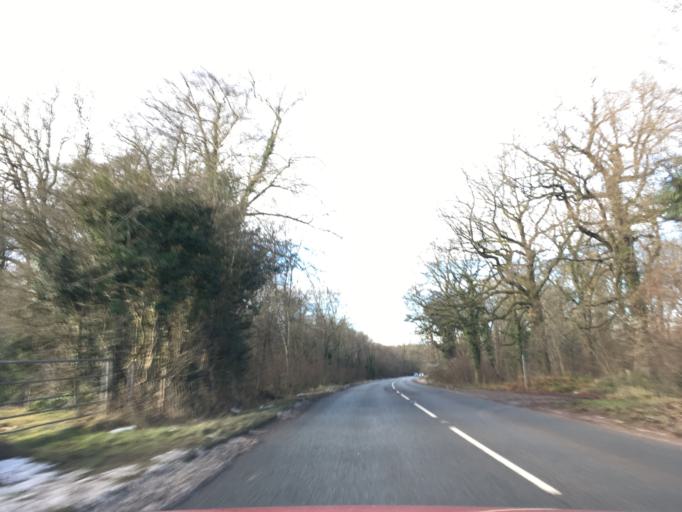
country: GB
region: England
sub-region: Gloucestershire
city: Coleford
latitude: 51.8025
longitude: -2.6298
